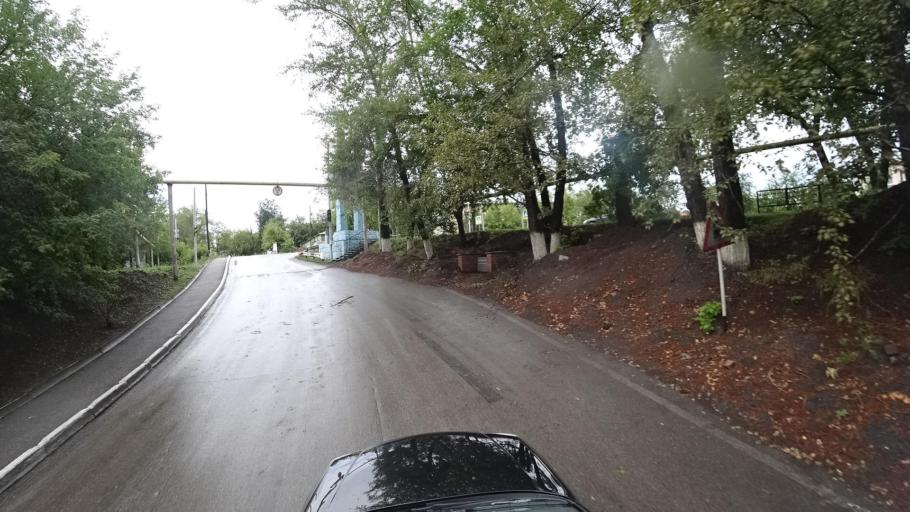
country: RU
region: Sverdlovsk
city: Kamyshlov
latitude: 56.8510
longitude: 62.7082
